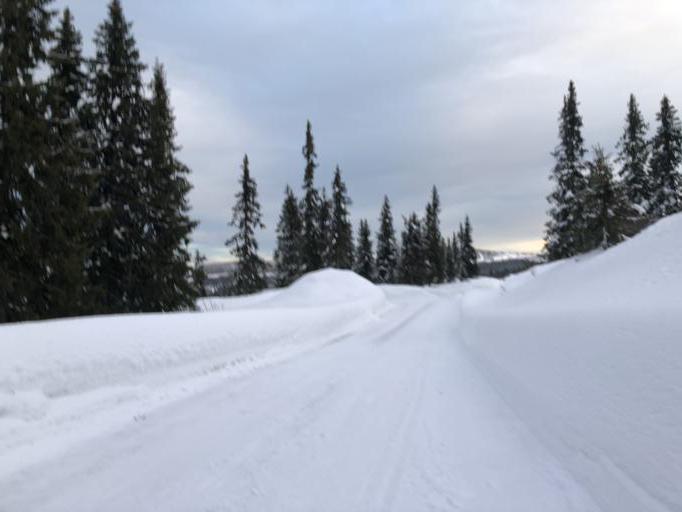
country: NO
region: Oppland
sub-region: Gausdal
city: Segalstad bru
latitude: 61.3314
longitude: 10.0514
